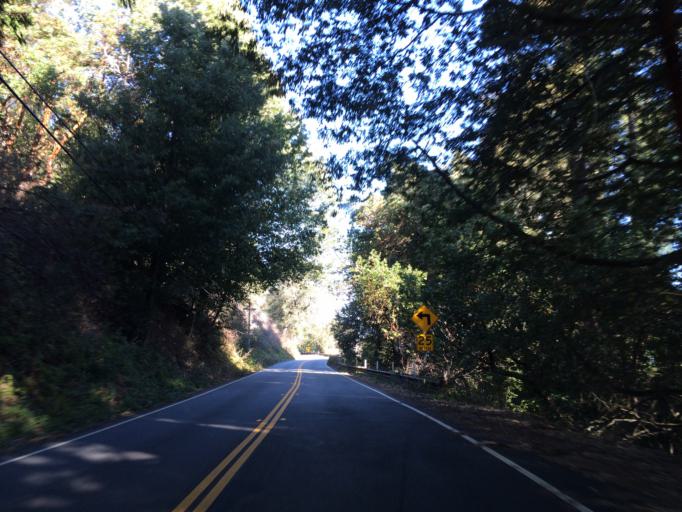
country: US
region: California
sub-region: Santa Cruz County
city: Boulder Creek
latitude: 37.1375
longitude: -122.1727
